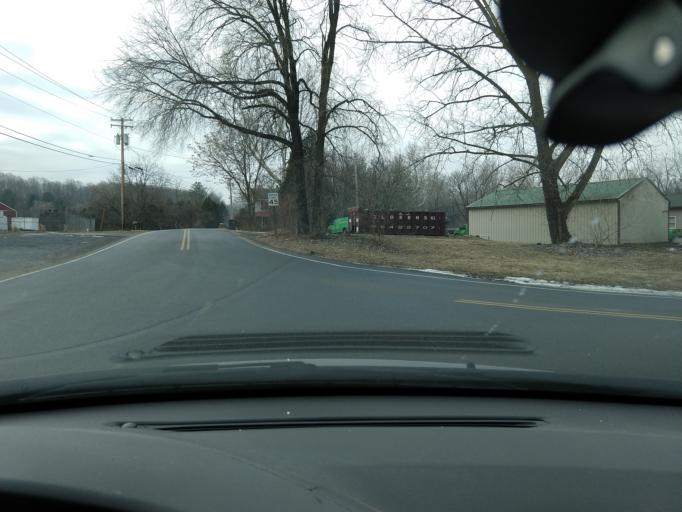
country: US
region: Pennsylvania
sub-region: Berks County
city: Birdsboro
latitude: 40.2561
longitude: -75.7680
